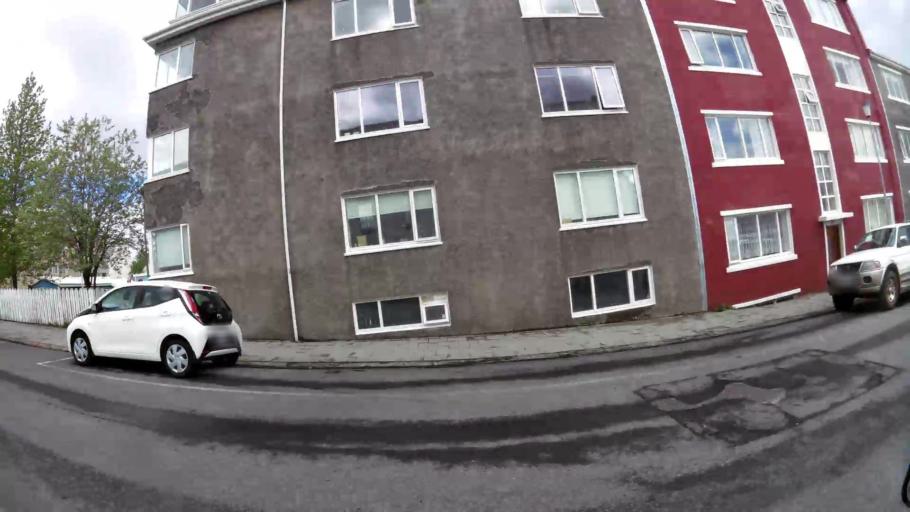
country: IS
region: Capital Region
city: Reykjavik
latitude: 64.1419
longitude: -21.9199
